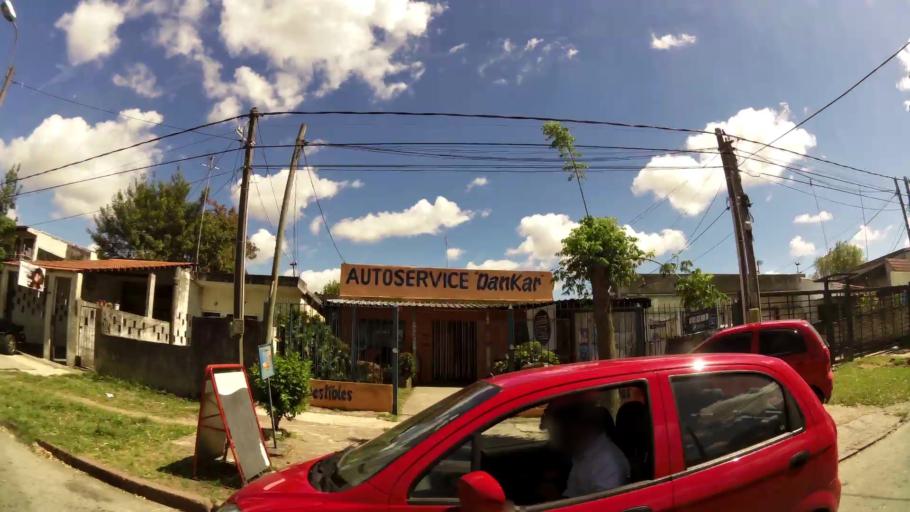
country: UY
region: Montevideo
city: Montevideo
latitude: -34.8401
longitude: -56.1370
